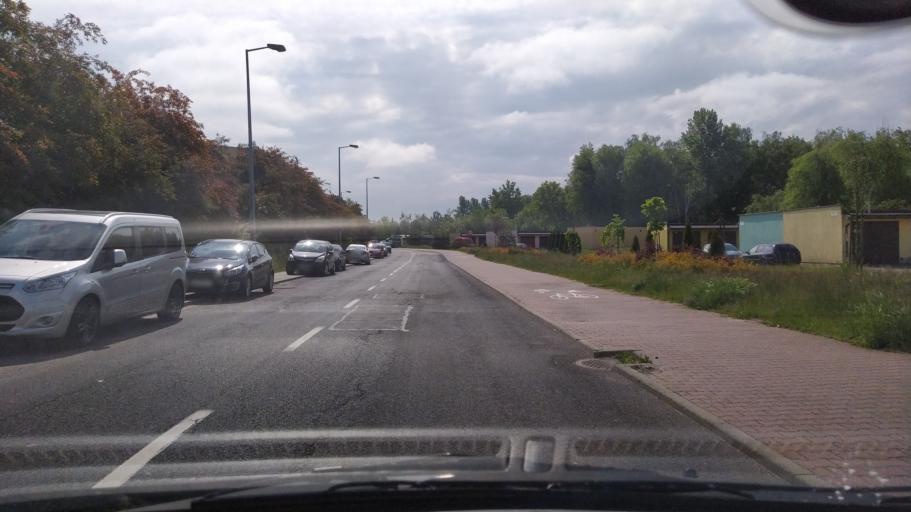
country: PL
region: Silesian Voivodeship
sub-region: Powiat gliwicki
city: Przyszowice
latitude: 50.2826
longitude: 18.7316
